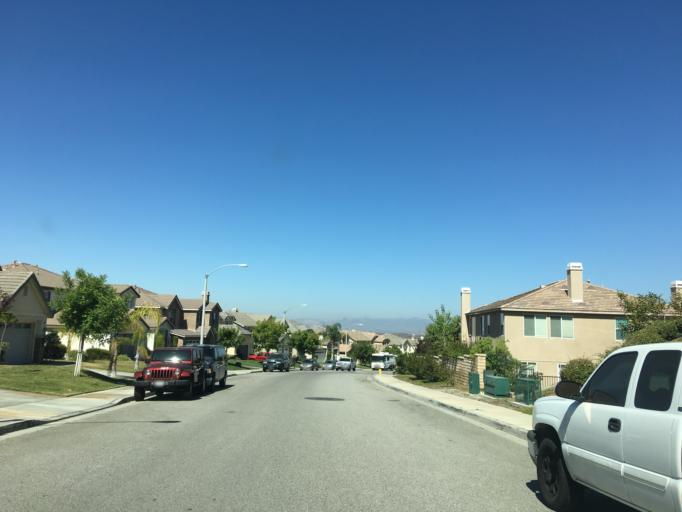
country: US
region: California
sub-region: Los Angeles County
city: Santa Clarita
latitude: 34.4478
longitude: -118.4781
